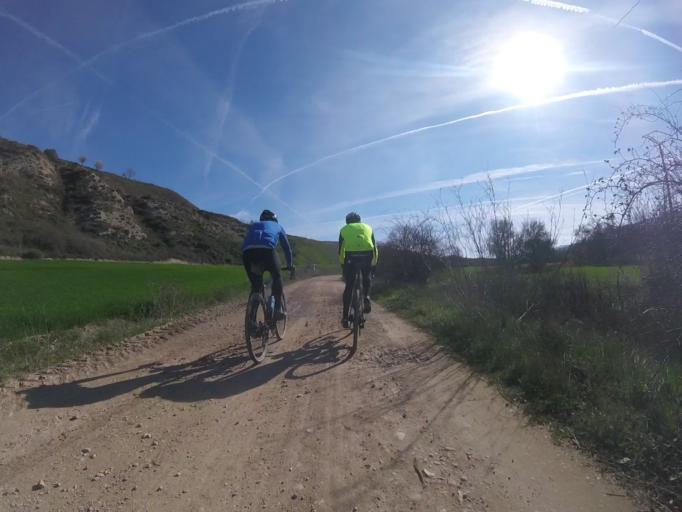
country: ES
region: Navarre
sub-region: Provincia de Navarra
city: Cirauqui
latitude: 42.6713
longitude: -1.9098
